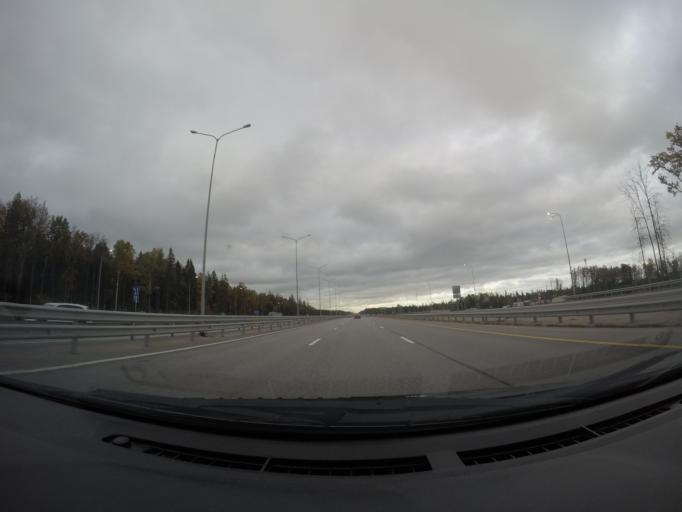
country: RU
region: Moskovskaya
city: Kubinka
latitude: 55.5840
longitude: 36.8230
